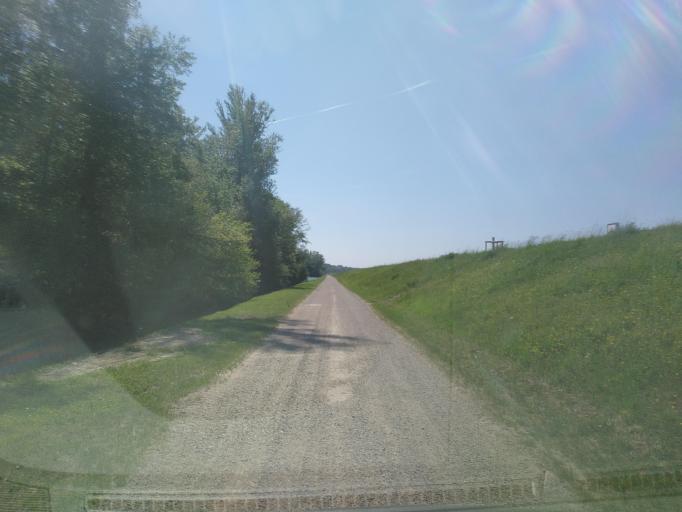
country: DE
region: Baden-Wuerttemberg
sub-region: Freiburg Region
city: Breisach am Rhein
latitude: 48.0697
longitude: 7.5730
